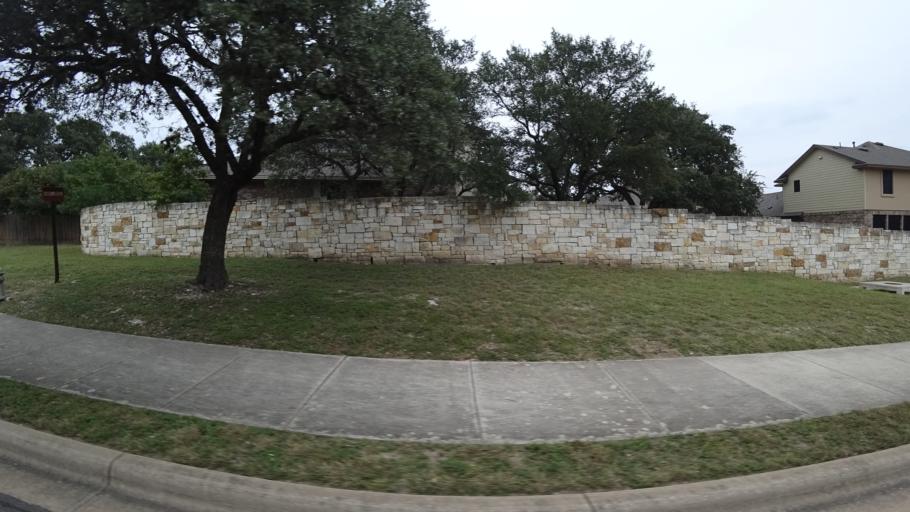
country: US
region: Texas
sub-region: Travis County
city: Shady Hollow
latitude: 30.2102
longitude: -97.8906
